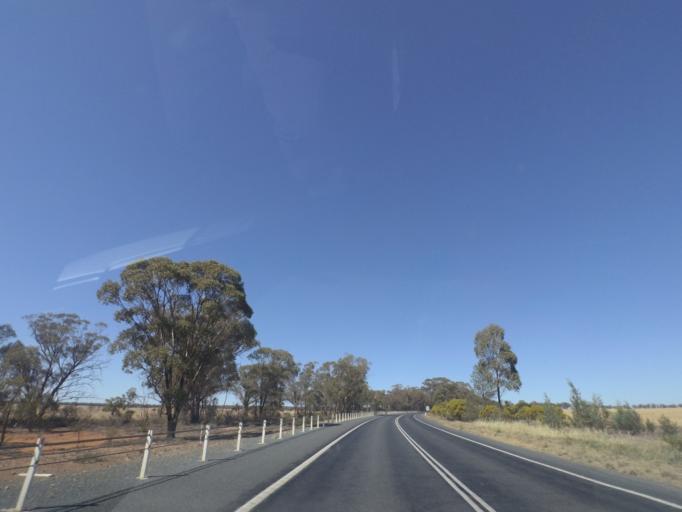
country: AU
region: New South Wales
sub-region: Bland
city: West Wyalong
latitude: -34.1129
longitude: 147.1385
